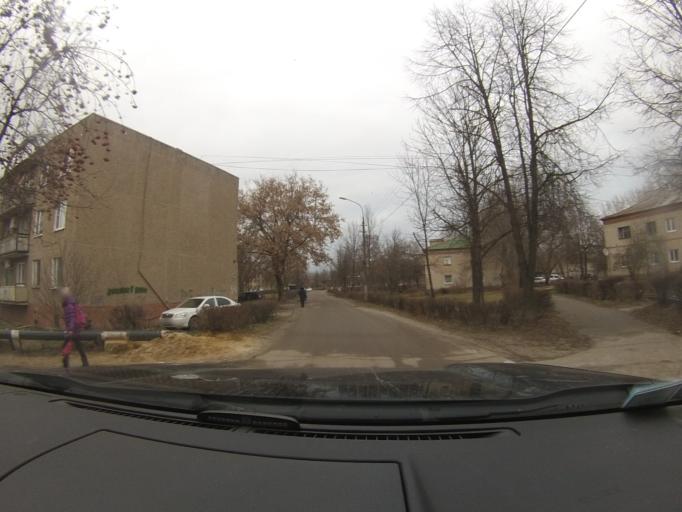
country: RU
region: Moskovskaya
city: Lopatinskiy
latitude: 55.3221
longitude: 38.7042
